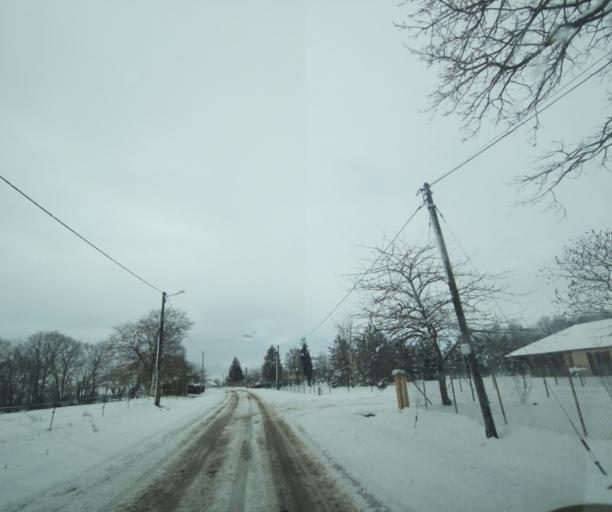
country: FR
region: Champagne-Ardenne
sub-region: Departement de la Haute-Marne
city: Montier-en-Der
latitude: 48.5254
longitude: 4.7196
